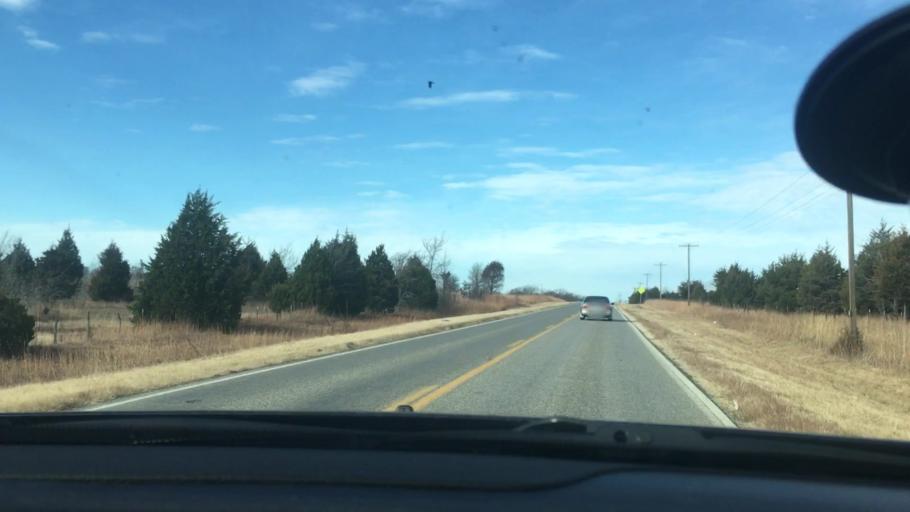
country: US
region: Oklahoma
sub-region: Seminole County
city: Konawa
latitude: 34.9450
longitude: -96.7246
